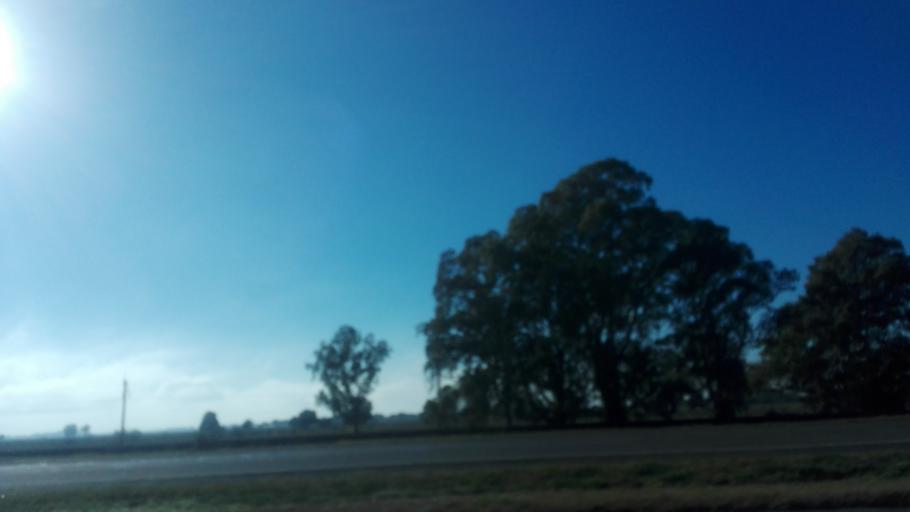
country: AR
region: Buenos Aires
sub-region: Partido de Chascomus
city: Chascomus
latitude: -35.7018
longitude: -57.9454
